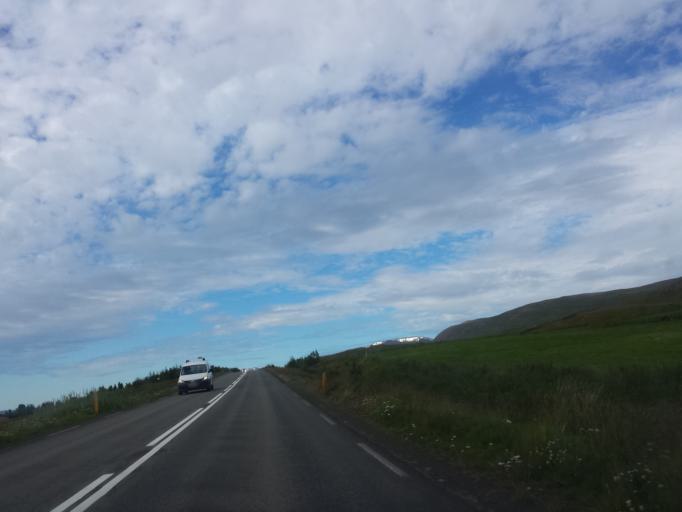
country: IS
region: Northeast
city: Akureyri
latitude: 65.7397
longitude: -18.0739
